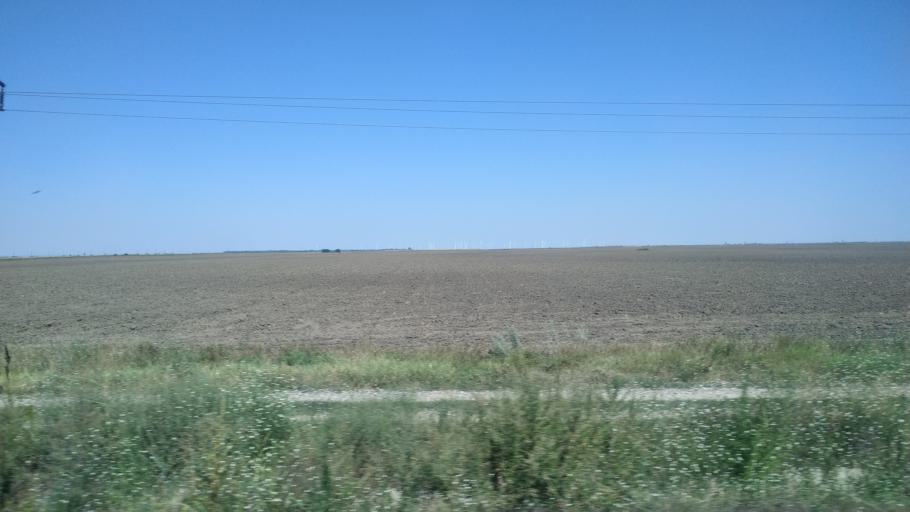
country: RO
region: Ialomita
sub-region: Municipiul Fetesti
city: Buliga
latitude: 44.4192
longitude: 27.7374
